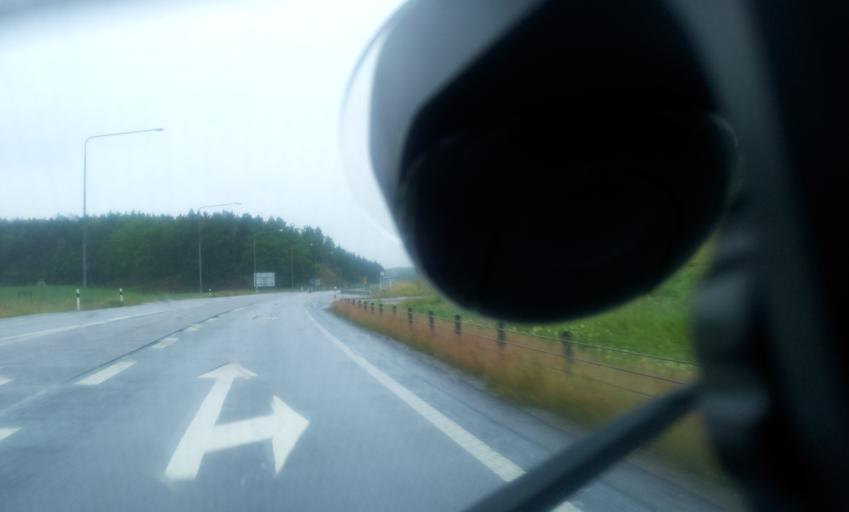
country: SE
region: OEstergoetland
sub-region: Valdemarsviks Kommun
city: Gusum
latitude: 58.3817
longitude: 16.4176
